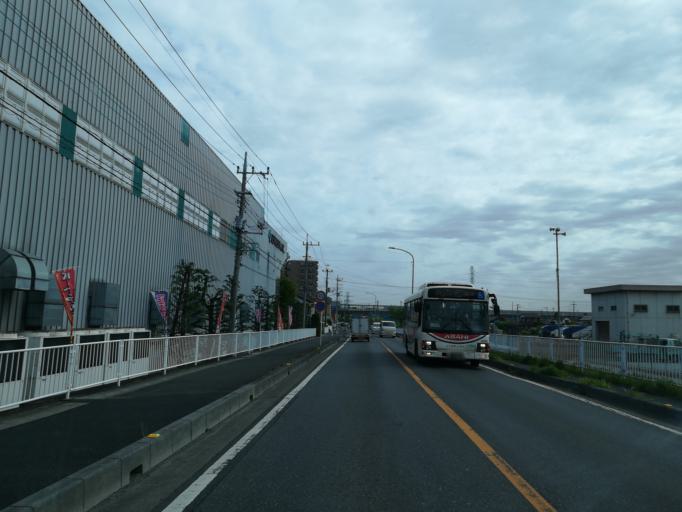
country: JP
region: Saitama
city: Satte
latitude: 36.0622
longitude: 139.7054
